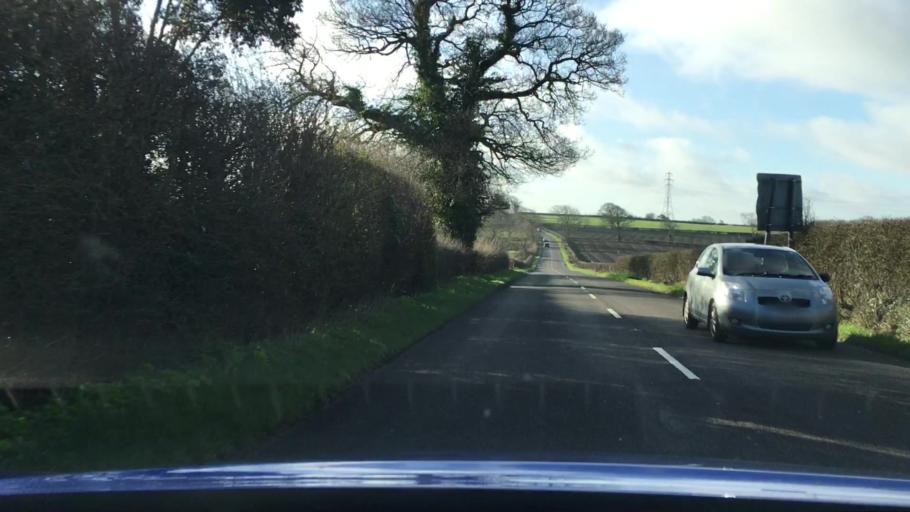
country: GB
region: England
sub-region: Derbyshire
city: Tibshelf
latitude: 53.1609
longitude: -1.3444
